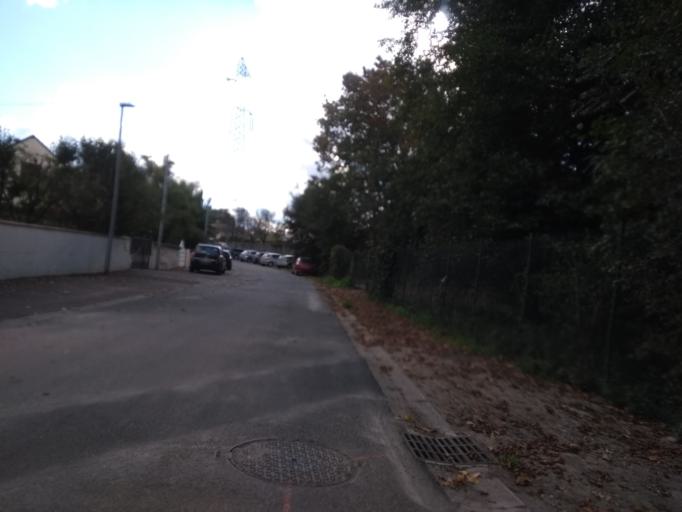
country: FR
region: Aquitaine
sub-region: Departement de la Gironde
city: Canejan
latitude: 44.7595
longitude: -0.6388
